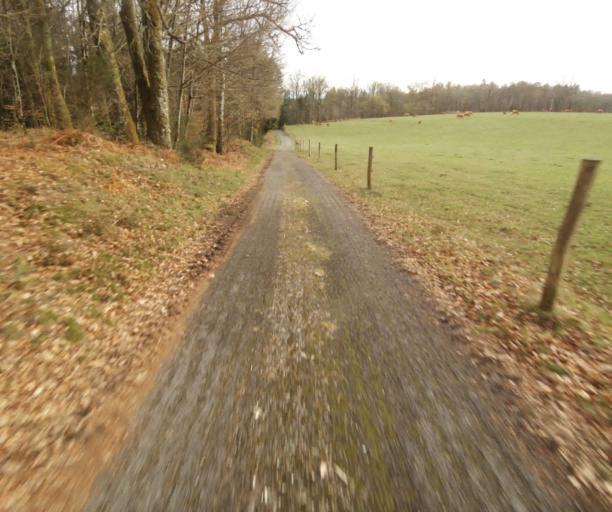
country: FR
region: Limousin
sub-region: Departement de la Correze
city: Saint-Privat
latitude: 45.2169
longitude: 1.9958
